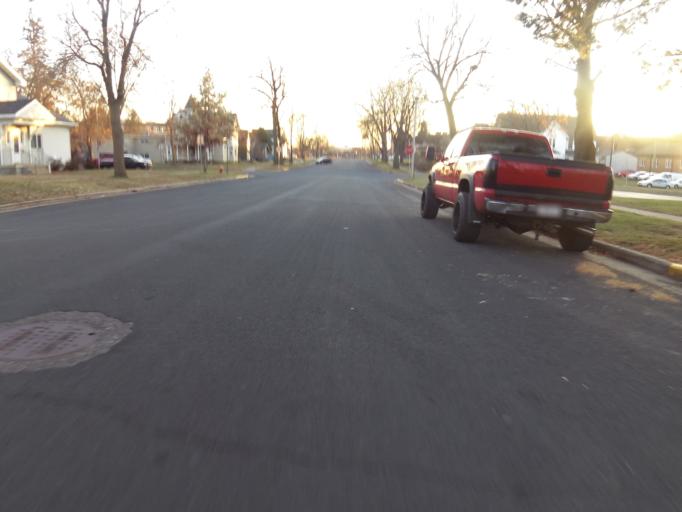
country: US
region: Wisconsin
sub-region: Pierce County
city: River Falls
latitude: 44.8573
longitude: -92.6234
